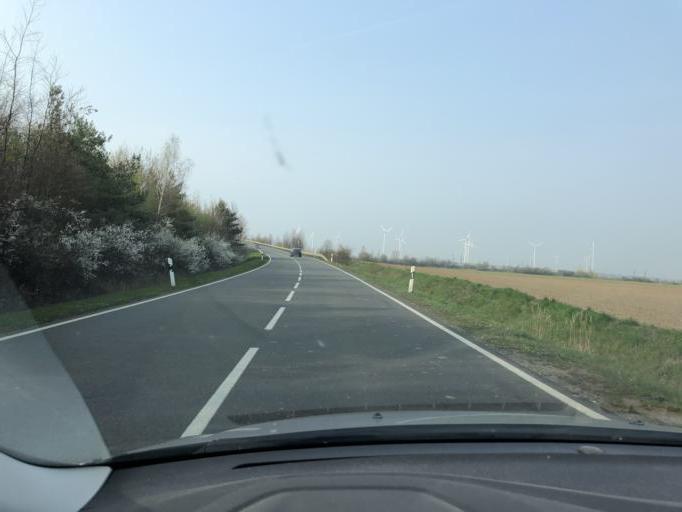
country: DE
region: Saxony-Anhalt
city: Brehna
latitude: 51.5539
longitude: 12.2312
